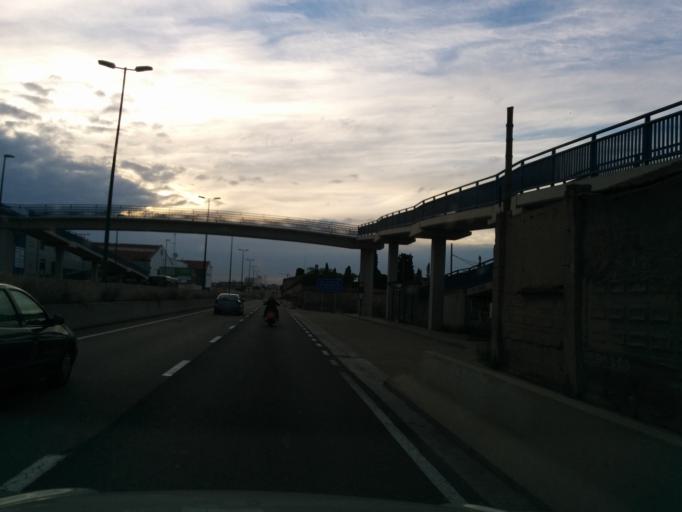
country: ES
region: Aragon
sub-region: Provincia de Zaragoza
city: Zaragoza
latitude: 41.6279
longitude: -0.8524
